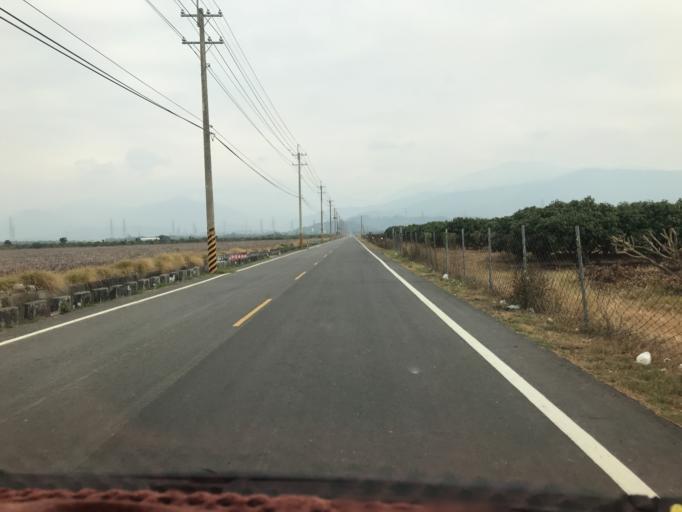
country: TW
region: Taiwan
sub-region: Pingtung
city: Pingtung
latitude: 22.4105
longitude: 120.5969
